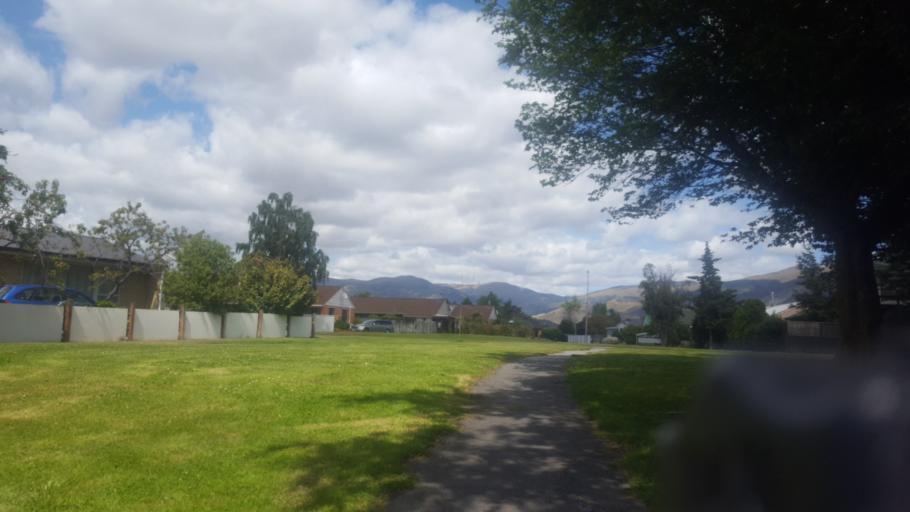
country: NZ
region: Otago
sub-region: Queenstown-Lakes District
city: Wanaka
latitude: -45.0411
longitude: 169.1849
